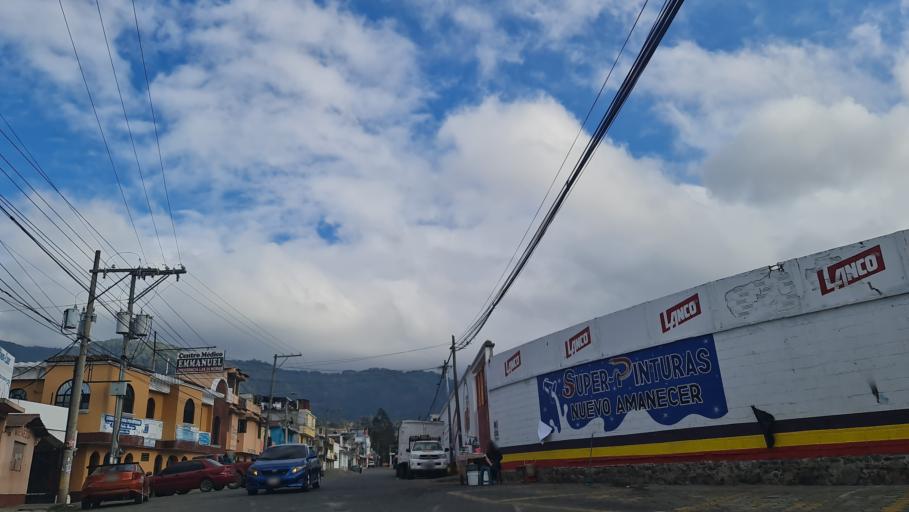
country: GT
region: San Marcos
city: San Pedro Sacatepequez
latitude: 14.9708
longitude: -91.7788
